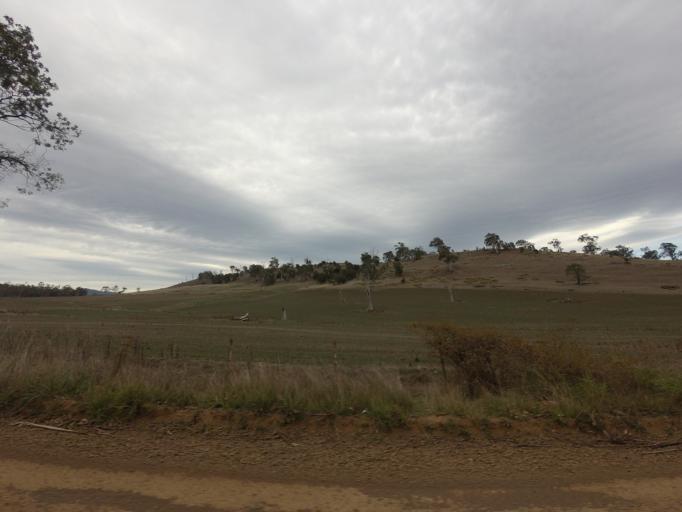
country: AU
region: Tasmania
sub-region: Derwent Valley
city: New Norfolk
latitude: -42.5637
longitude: 146.9312
